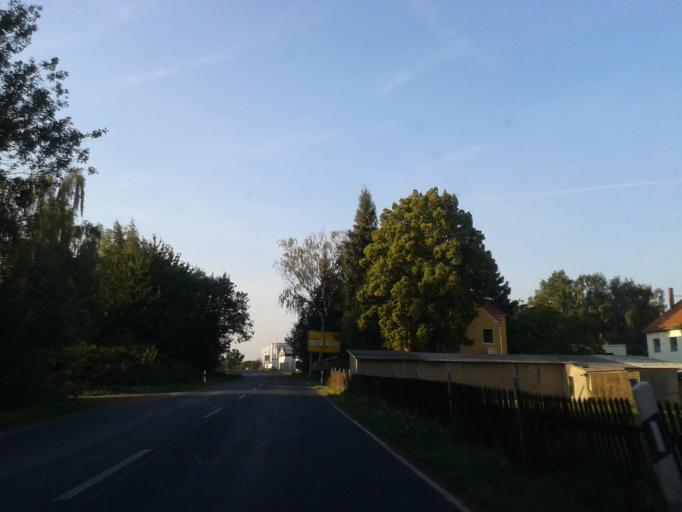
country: DE
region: Saxony
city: Klipphausen
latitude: 51.0955
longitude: 13.4966
